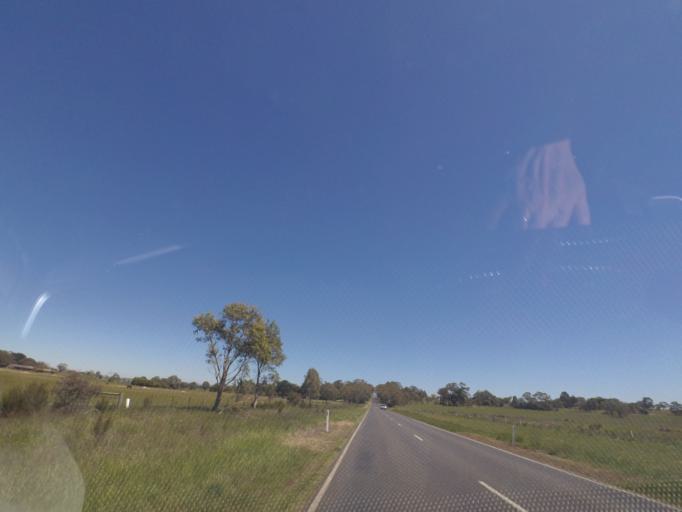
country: AU
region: Victoria
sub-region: Whittlesea
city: Whittlesea
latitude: -37.2922
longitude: 144.9165
